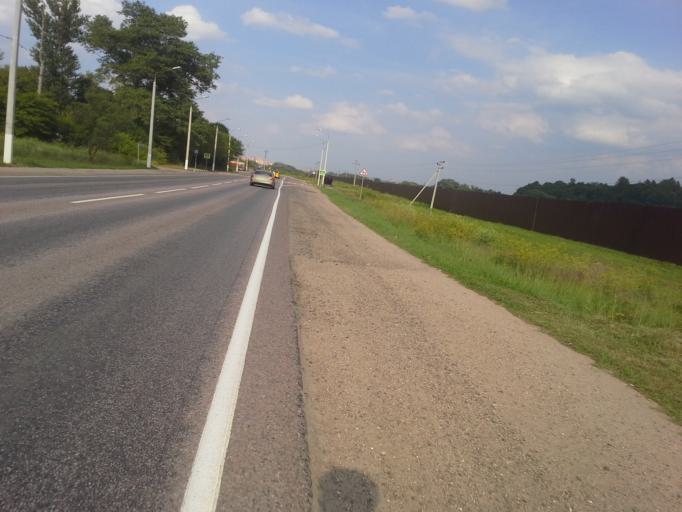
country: RU
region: Moskovskaya
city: Istra
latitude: 55.8991
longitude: 36.8040
